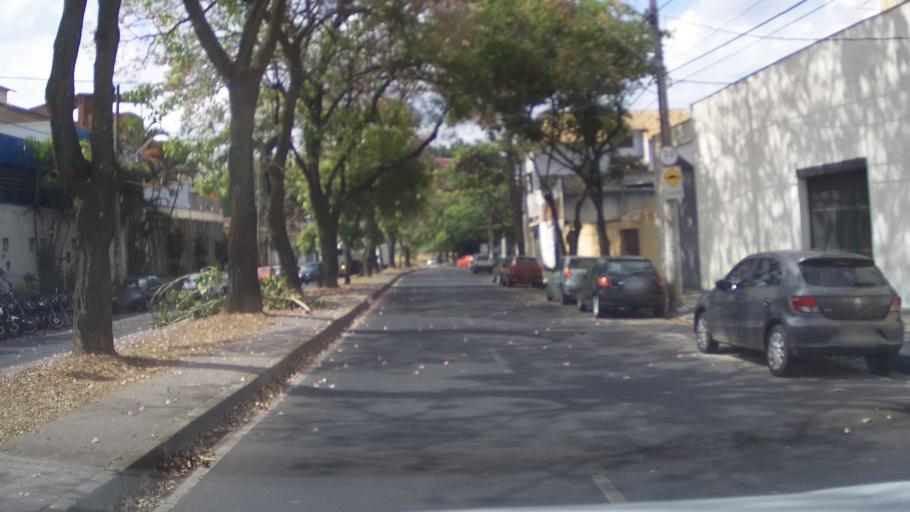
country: BR
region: Minas Gerais
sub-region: Belo Horizonte
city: Belo Horizonte
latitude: -19.8409
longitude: -43.9741
